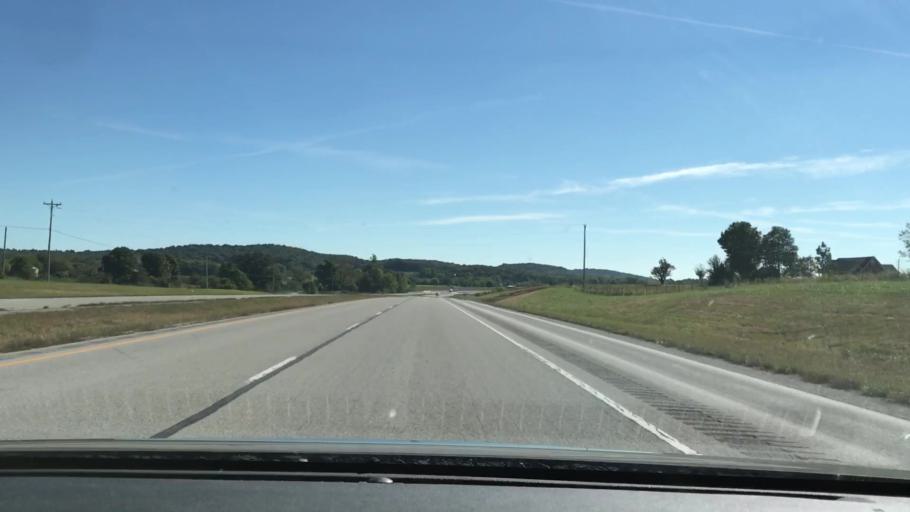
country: US
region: Kentucky
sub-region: Todd County
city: Elkton
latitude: 36.8406
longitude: -87.2523
